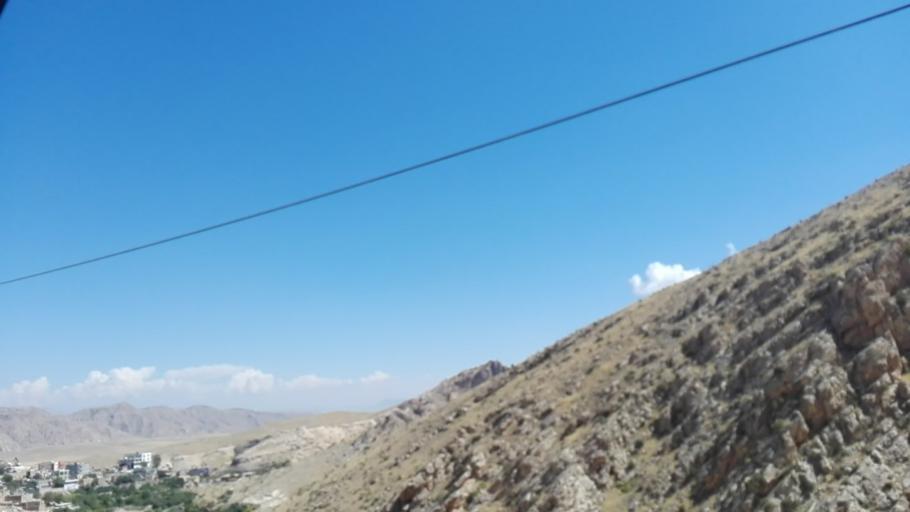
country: TR
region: Batman
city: Hasankeyf
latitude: 37.7012
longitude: 41.4609
